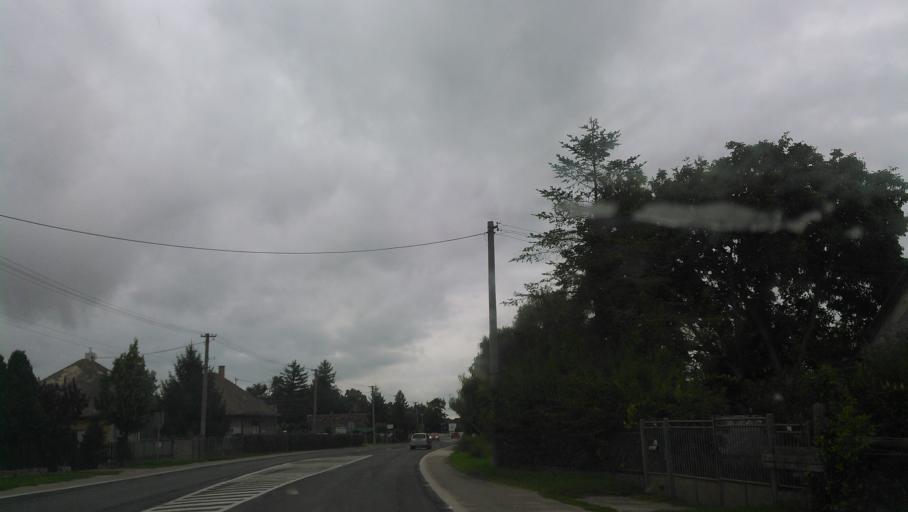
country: SK
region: Trnavsky
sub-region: Okres Dunajska Streda
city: Velky Meder
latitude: 47.9412
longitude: 17.7169
